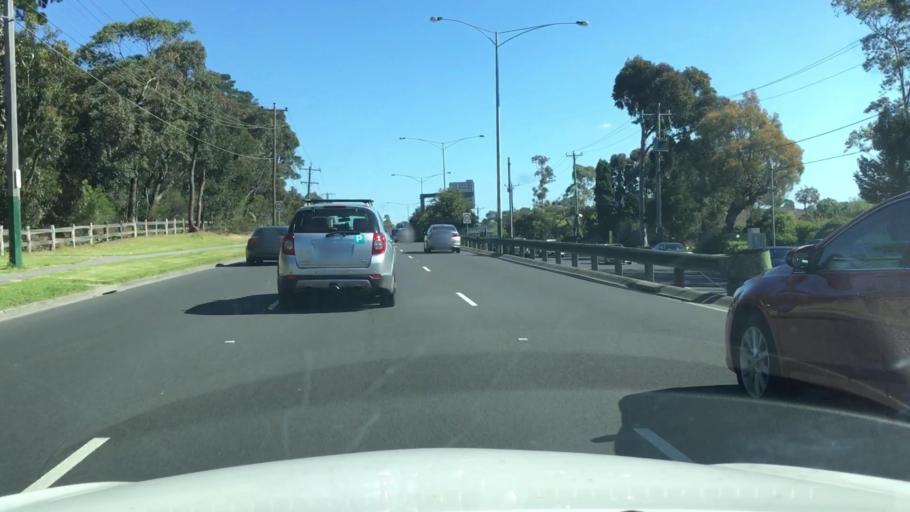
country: AU
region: Victoria
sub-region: Whitehorse
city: Nunawading
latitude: -37.8060
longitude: 145.1779
